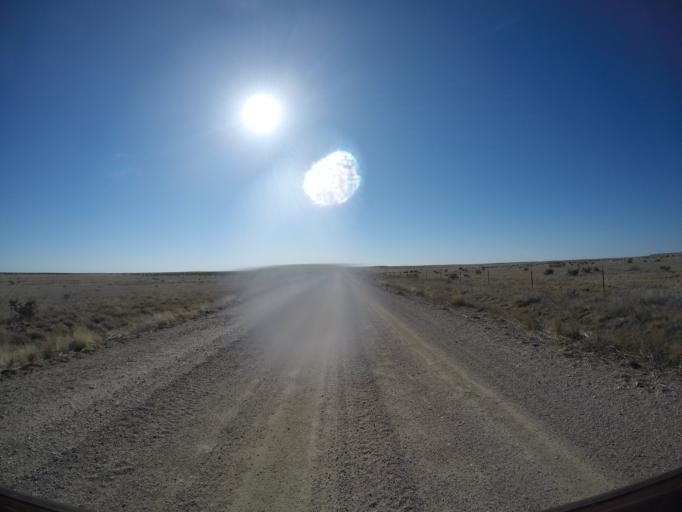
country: US
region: Colorado
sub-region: Otero County
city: La Junta
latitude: 37.7045
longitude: -103.6204
